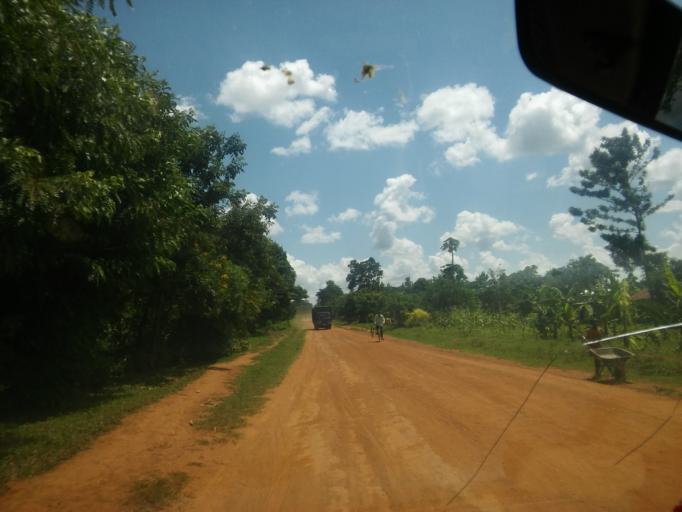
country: UG
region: Eastern Region
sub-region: Budaka District
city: Budaka
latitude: 1.1125
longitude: 33.9546
